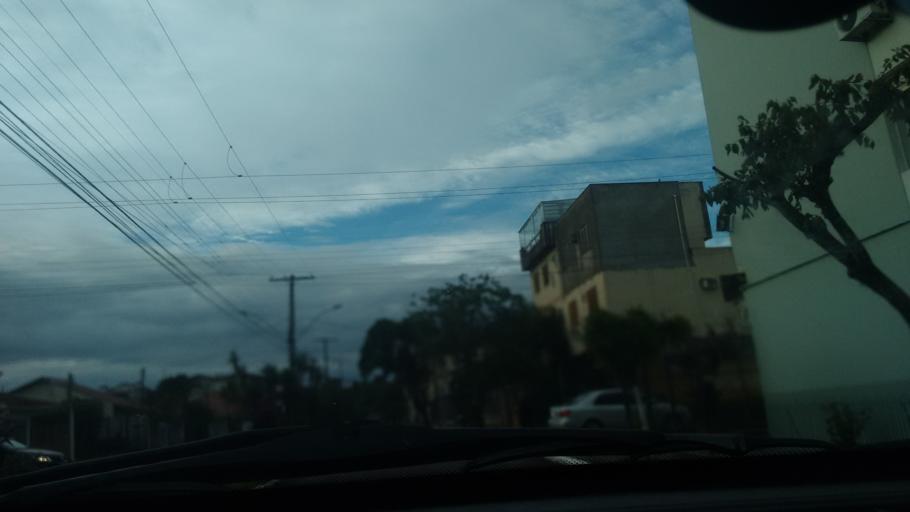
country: BR
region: Rio Grande do Sul
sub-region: Cachoeirinha
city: Cachoeirinha
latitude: -30.0000
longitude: -51.1462
